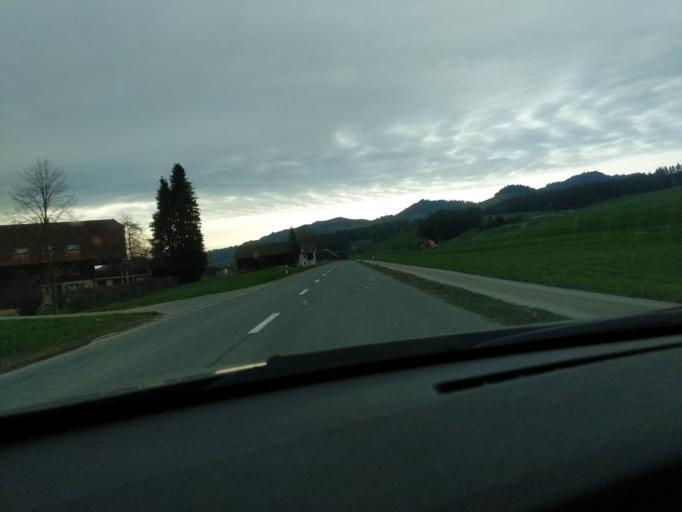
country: CH
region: Lucerne
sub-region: Entlebuch District
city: Schuepfheim
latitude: 46.9362
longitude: 7.9952
